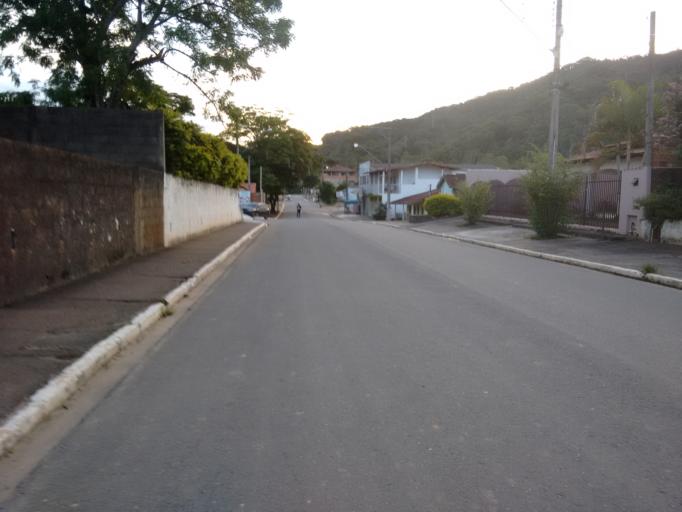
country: BR
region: Sao Paulo
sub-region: Apiai
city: Apiai
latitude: -24.5864
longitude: -48.5949
